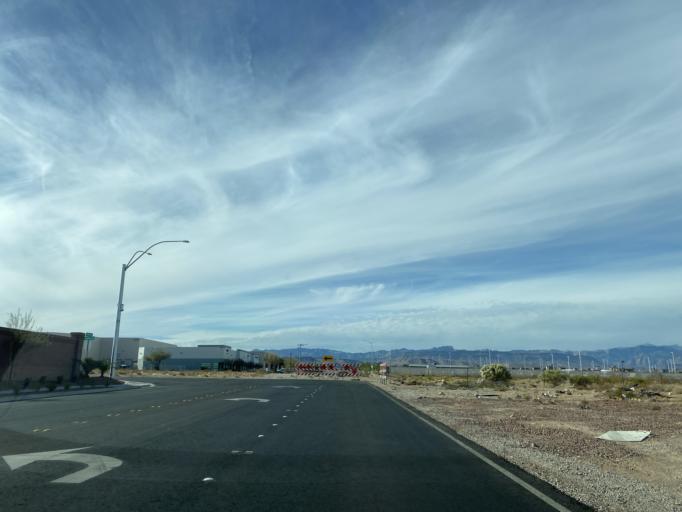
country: US
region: Nevada
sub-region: Clark County
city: Enterprise
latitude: 36.0617
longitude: -115.2331
